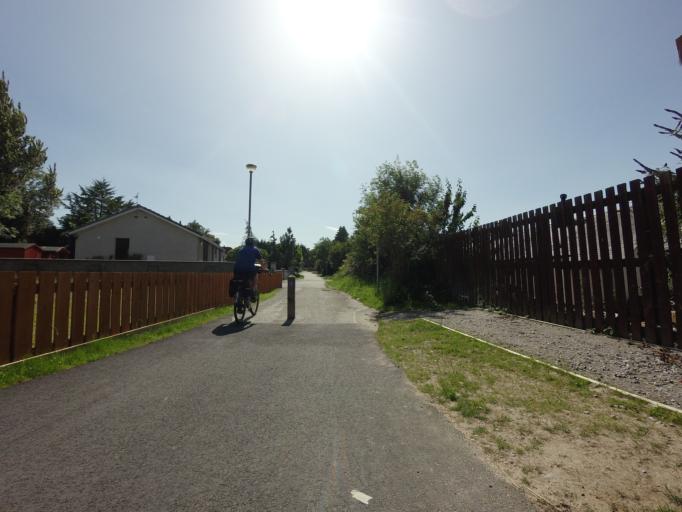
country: GB
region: Scotland
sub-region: Highland
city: Inverness
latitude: 57.4834
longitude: -4.1466
